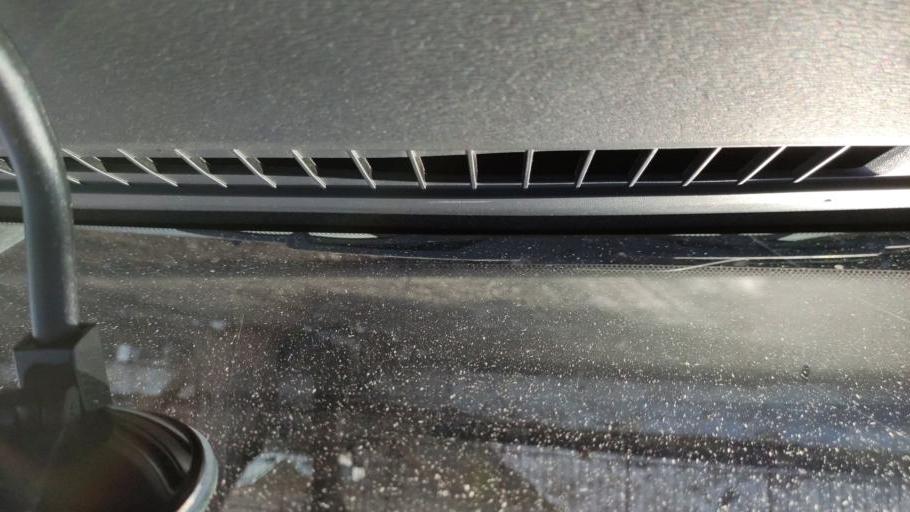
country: RU
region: Samara
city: Samara
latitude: 53.2025
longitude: 50.0990
